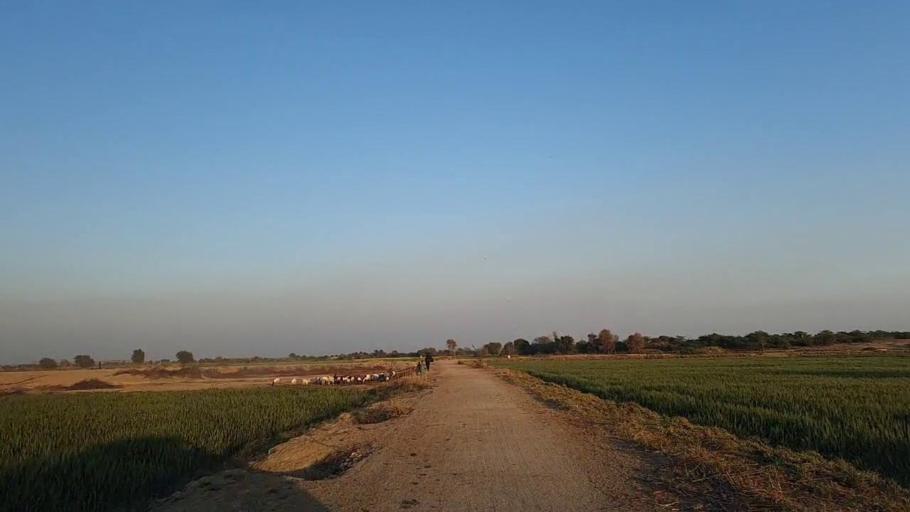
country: PK
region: Sindh
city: Jam Sahib
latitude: 26.3258
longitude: 68.6282
